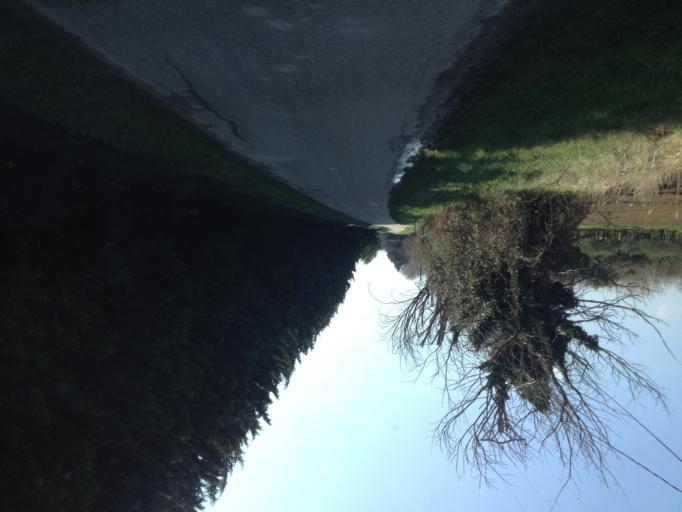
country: FR
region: Provence-Alpes-Cote d'Azur
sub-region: Departement du Vaucluse
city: Jonquieres
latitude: 44.1150
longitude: 4.9168
